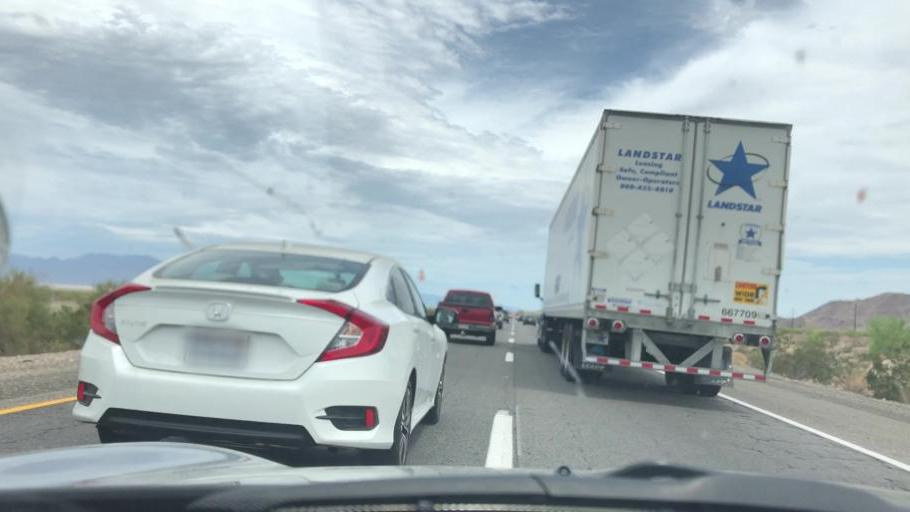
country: US
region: California
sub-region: Imperial County
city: Niland
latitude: 33.7096
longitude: -115.3725
